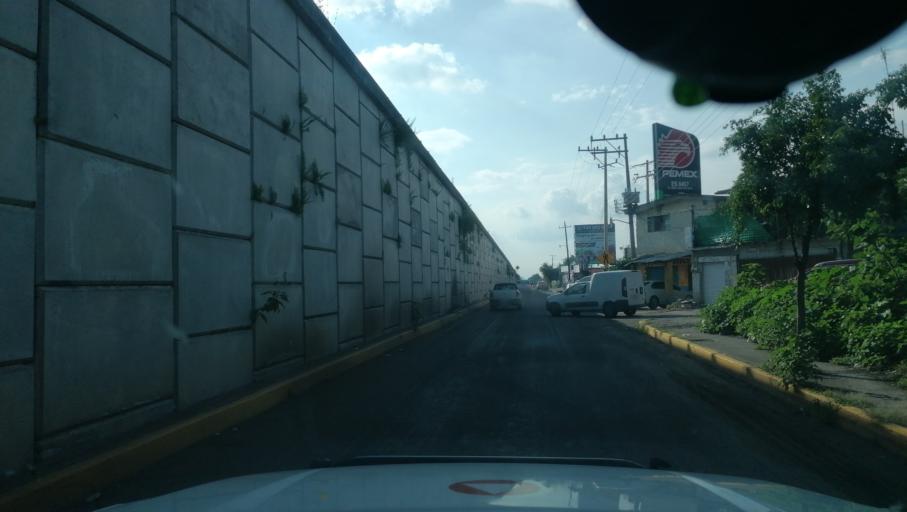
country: MX
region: Morelos
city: Amayuca
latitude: 18.7181
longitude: -98.7956
